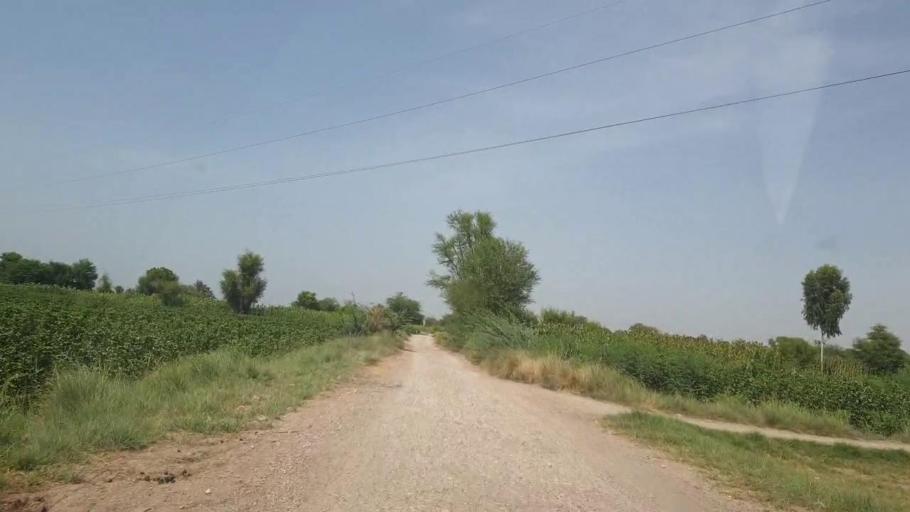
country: PK
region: Sindh
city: Bozdar
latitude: 27.0865
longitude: 68.6020
